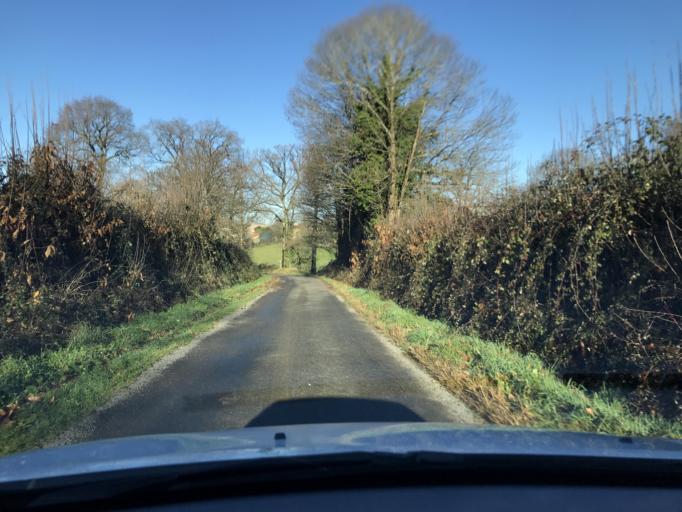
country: FR
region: Poitou-Charentes
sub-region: Departement de la Charente
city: Chasseneuil-sur-Bonnieure
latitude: 45.8419
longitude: 0.5191
